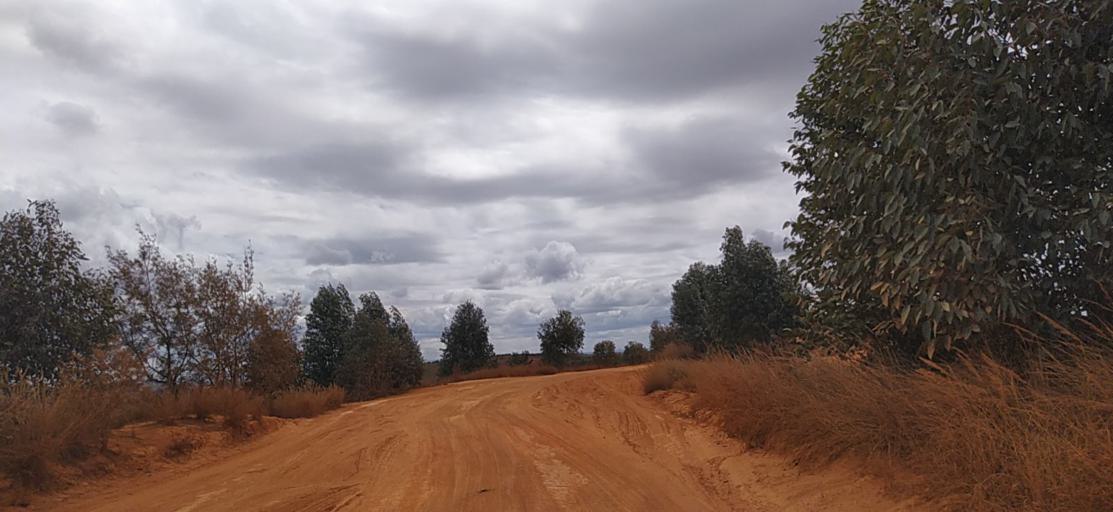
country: MG
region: Alaotra Mangoro
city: Ambatondrazaka
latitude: -18.0467
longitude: 48.2492
